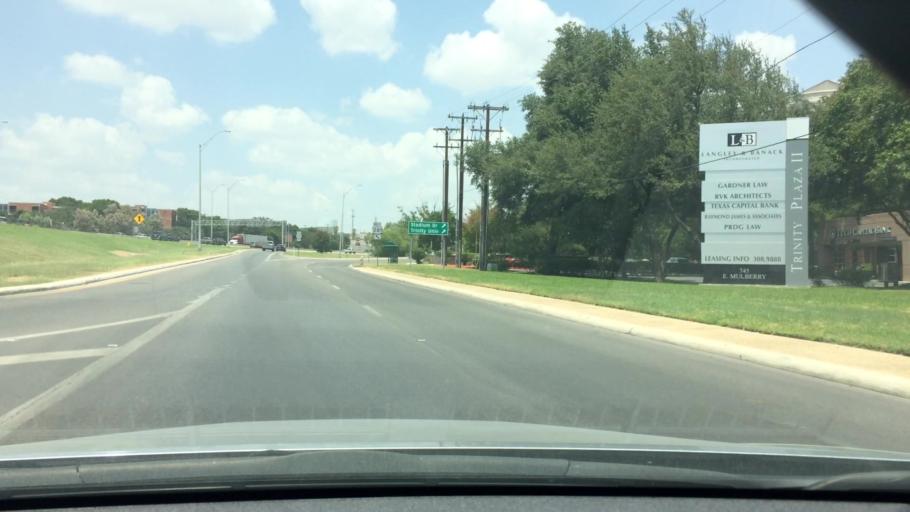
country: US
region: Texas
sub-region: Bexar County
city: Olmos Park
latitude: 29.4570
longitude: -98.4813
